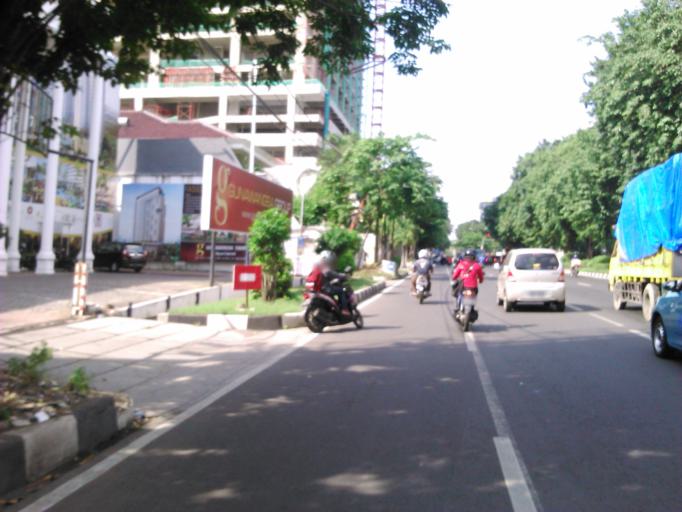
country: ID
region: East Java
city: Mulyorejo
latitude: -7.2787
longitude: 112.7811
